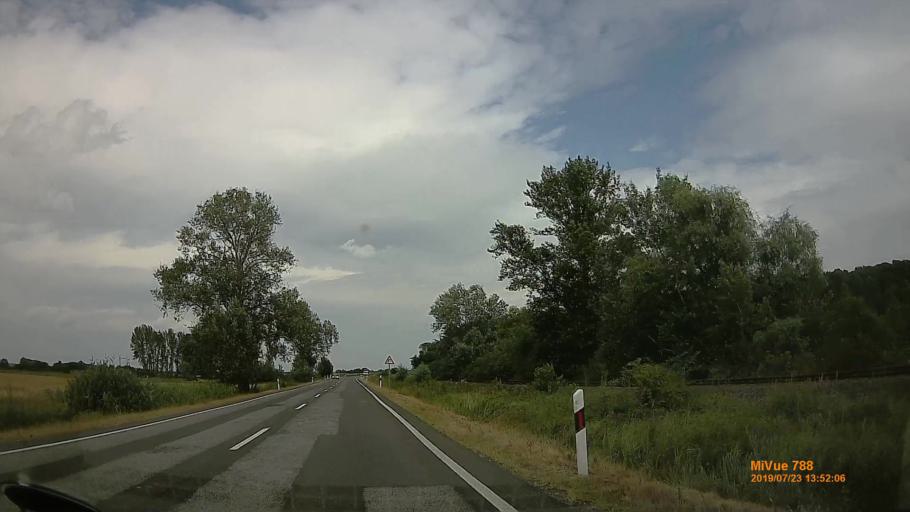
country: HU
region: Hajdu-Bihar
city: Polgar
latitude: 47.8980
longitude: 21.1566
